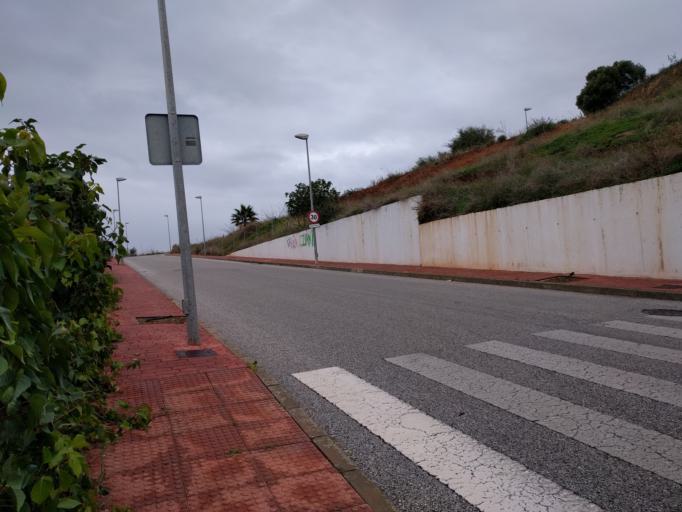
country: ES
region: Andalusia
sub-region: Provincia de Malaga
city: Fuengirola
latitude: 36.5047
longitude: -4.6871
